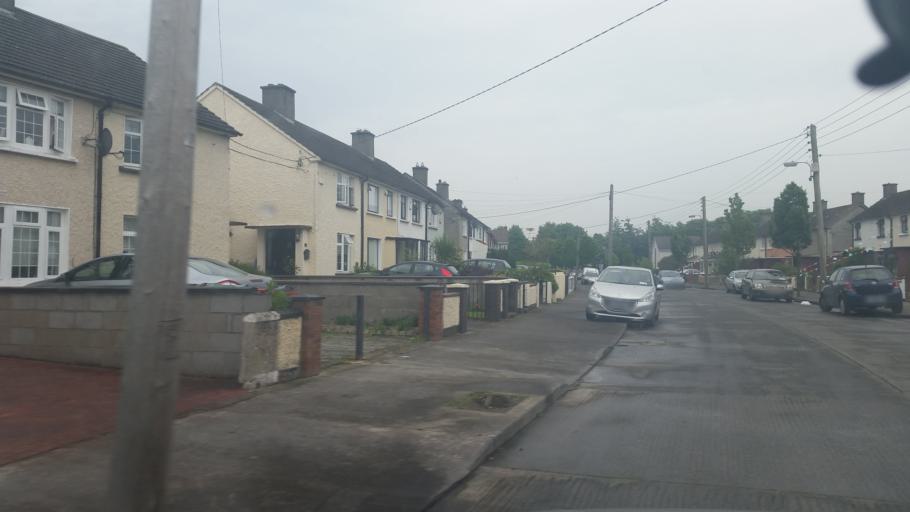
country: IE
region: Leinster
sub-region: Dublin City
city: Finglas
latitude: 53.3866
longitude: -6.3150
